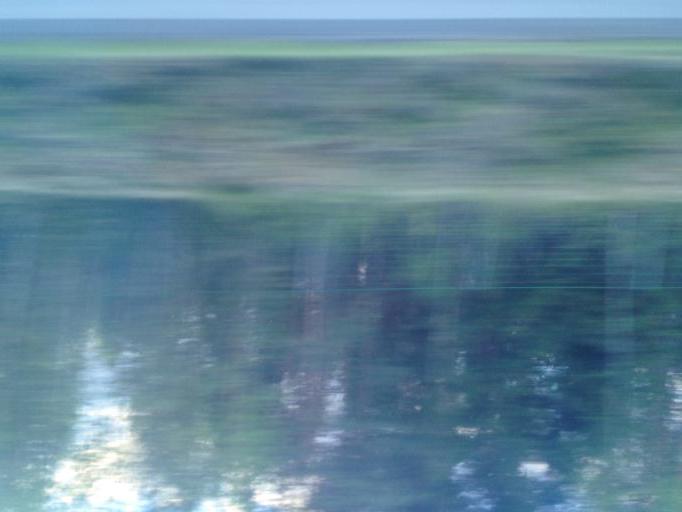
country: FI
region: Haeme
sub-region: Haemeenlinna
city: Kalvola
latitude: 61.1075
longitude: 24.1456
